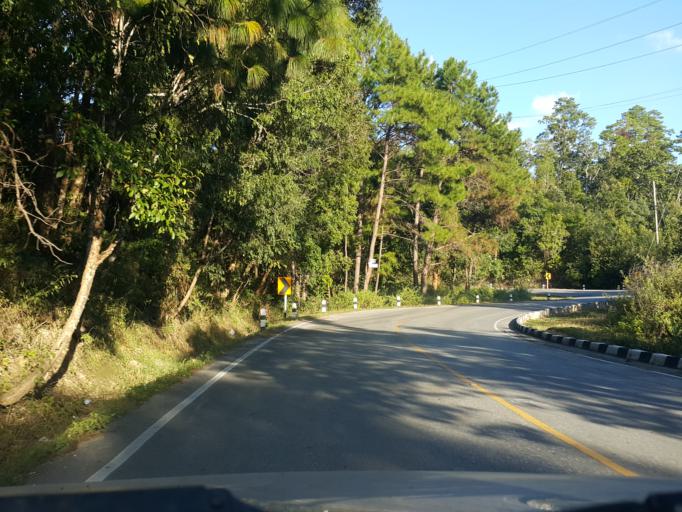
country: TH
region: Mae Hong Son
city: Mae Hi
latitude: 19.2728
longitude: 98.5477
